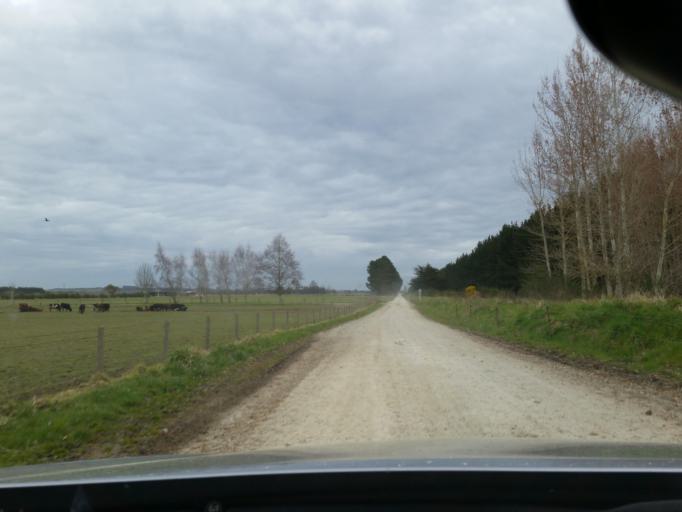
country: NZ
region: Southland
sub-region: Southland District
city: Winton
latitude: -46.2141
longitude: 168.4993
